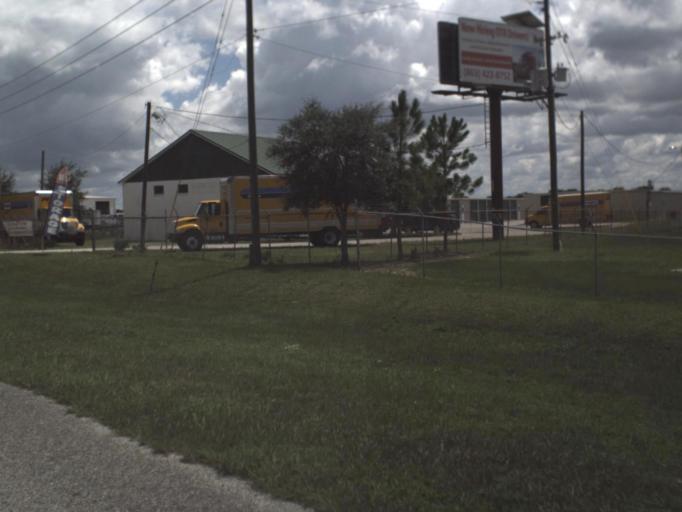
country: US
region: Florida
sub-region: Polk County
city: Babson Park
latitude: 27.8923
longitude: -81.4800
